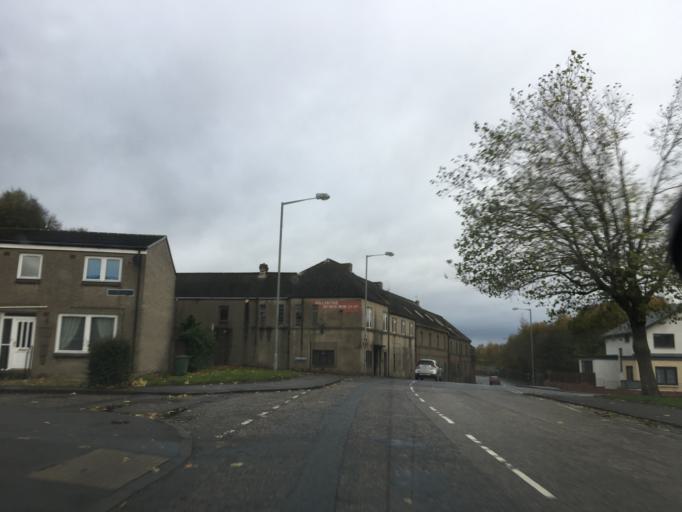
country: GB
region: Scotland
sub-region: Falkirk
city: Bo'ness
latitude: 56.0160
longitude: -3.5960
